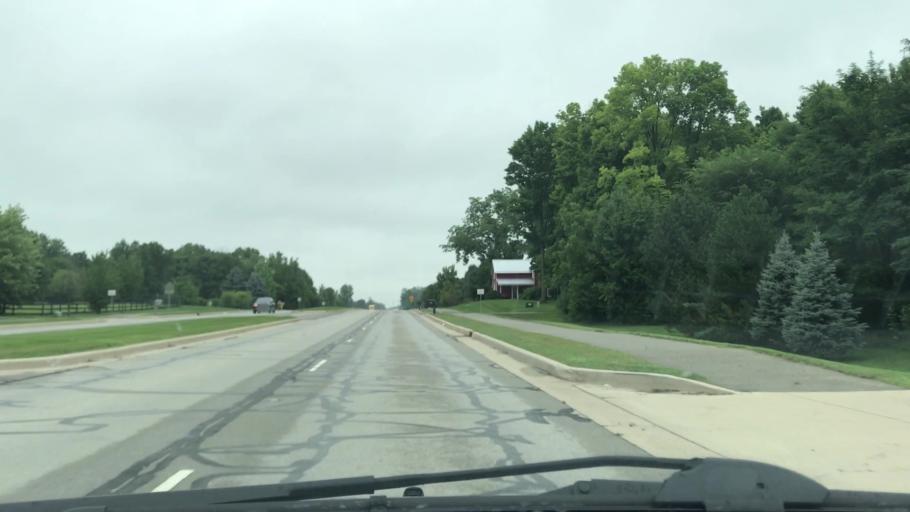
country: US
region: Indiana
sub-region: Hamilton County
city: Carmel
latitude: 40.0160
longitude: -86.0705
